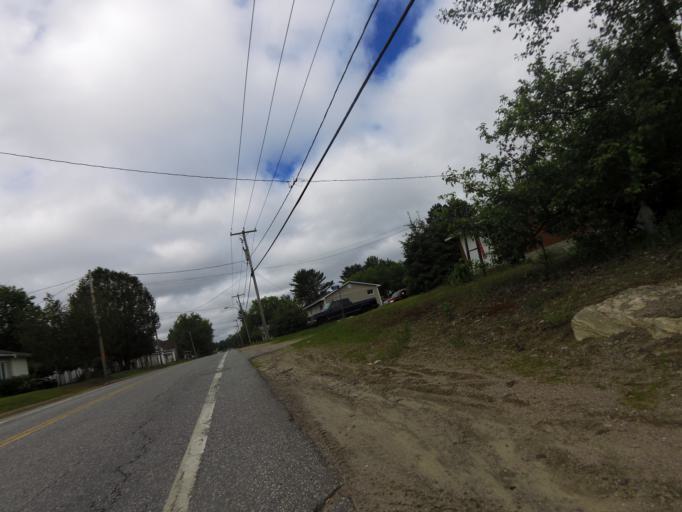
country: CA
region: Quebec
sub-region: Outaouais
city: Shawville
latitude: 45.8433
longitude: -76.4366
